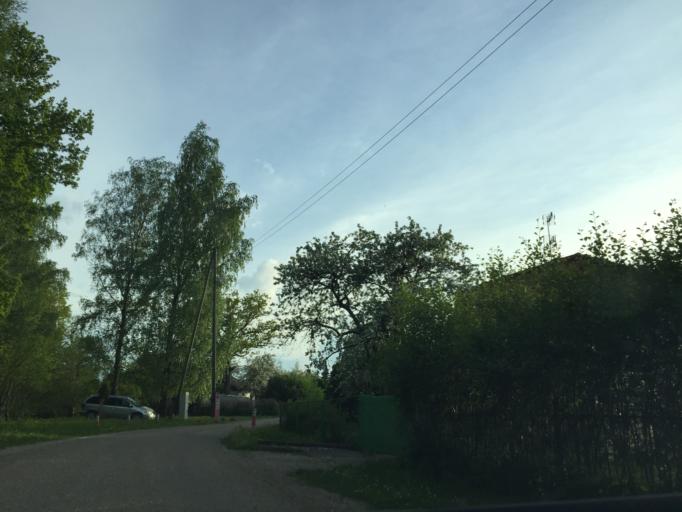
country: LV
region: Ozolnieku
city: Ozolnieki
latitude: 56.6570
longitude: 23.7714
